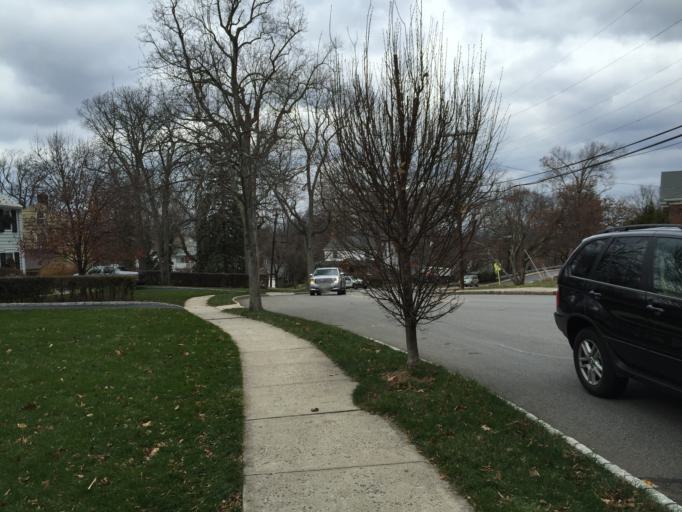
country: US
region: New Jersey
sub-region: Union County
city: Summit
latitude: 40.7168
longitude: -74.3707
